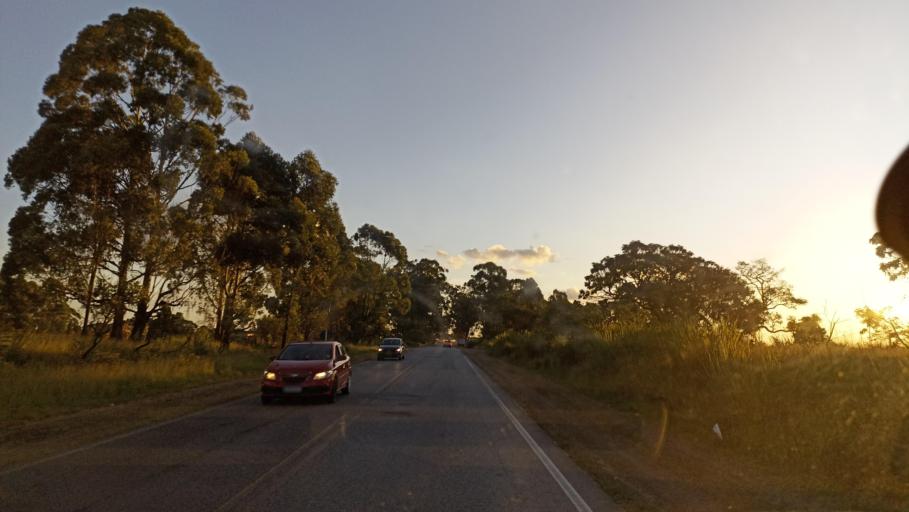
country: BR
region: Minas Gerais
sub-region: Sao Joao Del Rei
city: Sao Joao del Rei
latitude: -21.2395
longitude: -44.3995
